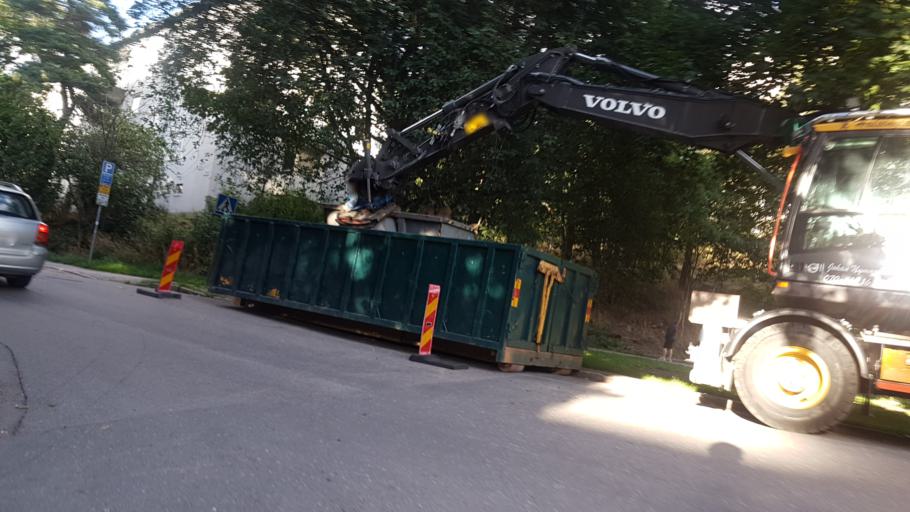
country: SE
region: Stockholm
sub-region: Stockholms Kommun
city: OEstermalm
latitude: 59.2926
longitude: 18.1101
